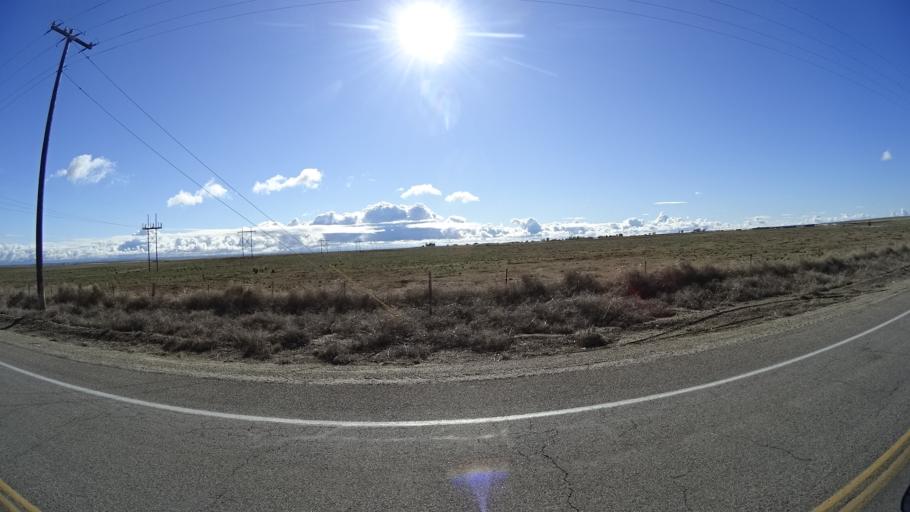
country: US
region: Idaho
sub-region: Ada County
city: Kuna
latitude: 43.4216
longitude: -116.4139
